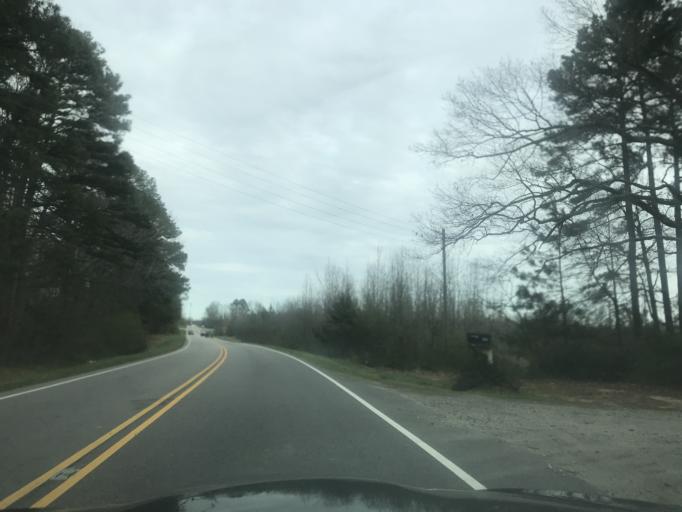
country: US
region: North Carolina
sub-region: Franklin County
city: Franklinton
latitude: 36.0945
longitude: -78.4142
